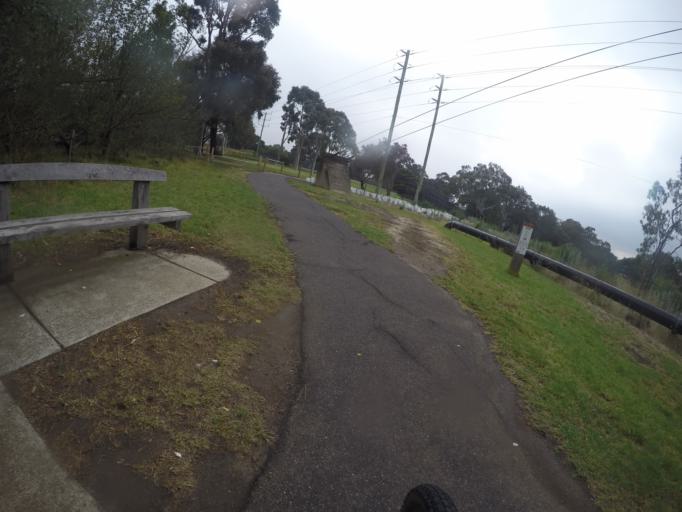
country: AU
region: Victoria
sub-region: Greater Geelong
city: Hamlyn Heights
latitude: -38.1443
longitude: 144.3175
